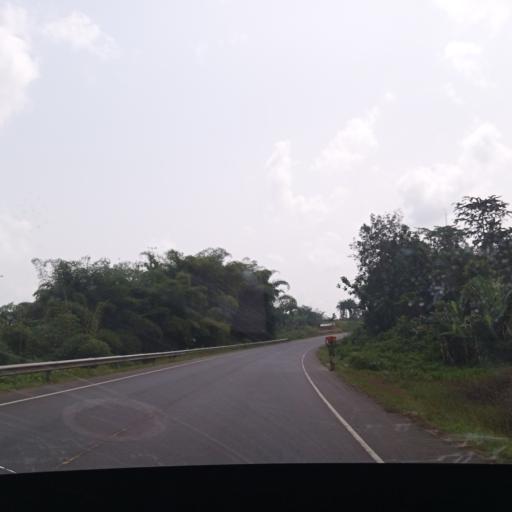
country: LR
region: Margibi
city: Kakata
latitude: 6.2410
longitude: -10.2856
